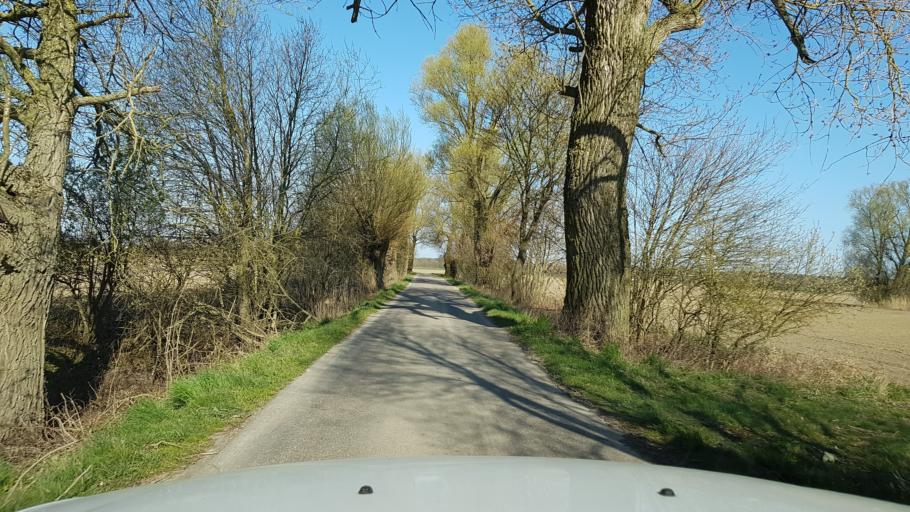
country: PL
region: West Pomeranian Voivodeship
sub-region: Powiat kolobrzeski
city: Ustronie Morskie
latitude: 54.2227
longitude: 15.8434
